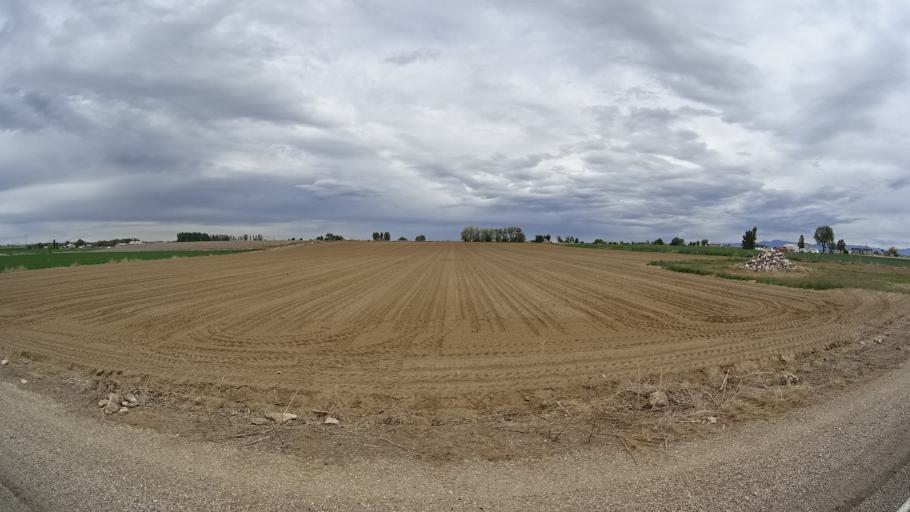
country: US
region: Idaho
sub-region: Canyon County
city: Nampa
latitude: 43.4592
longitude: -116.5179
